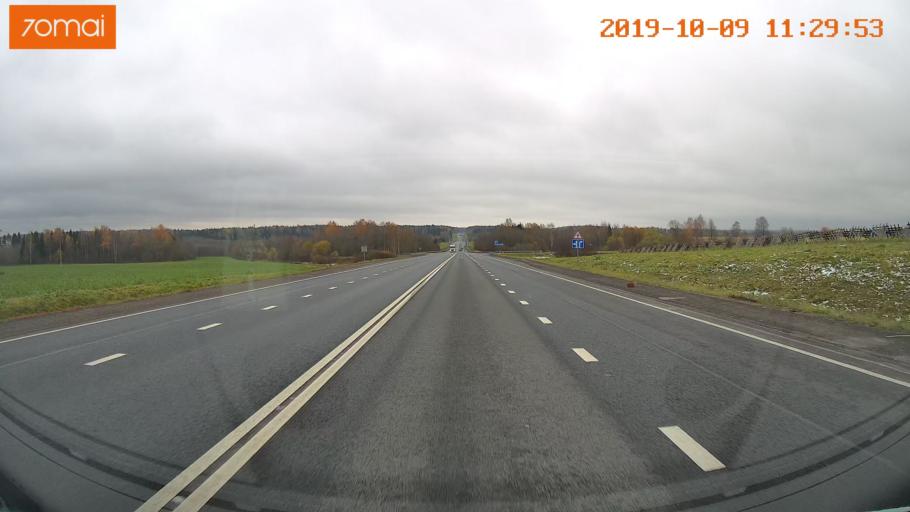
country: RU
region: Vologda
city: Vologda
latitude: 59.0585
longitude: 40.0632
